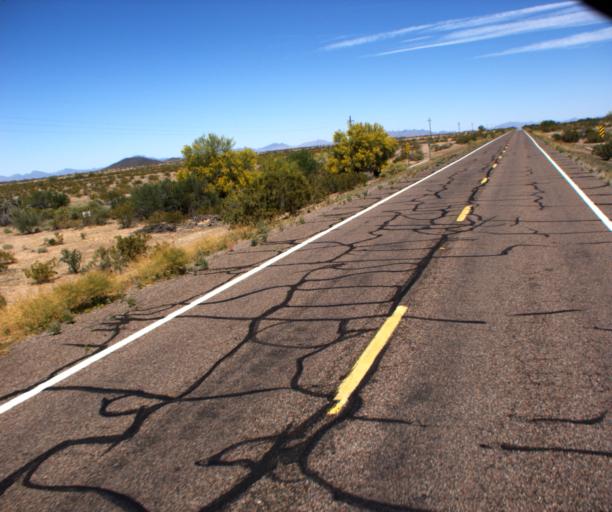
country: US
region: Arizona
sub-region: Maricopa County
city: Gila Bend
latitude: 32.7850
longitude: -112.8080
